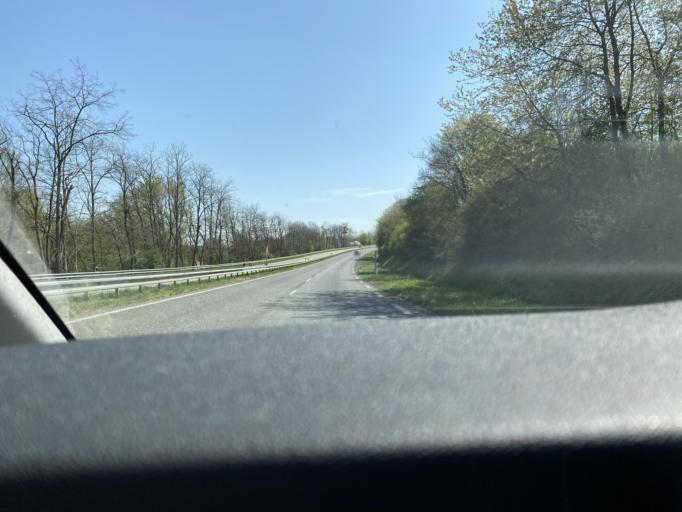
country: FR
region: Lorraine
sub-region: Departement de la Moselle
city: Kerbach
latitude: 49.1562
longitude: 6.9723
